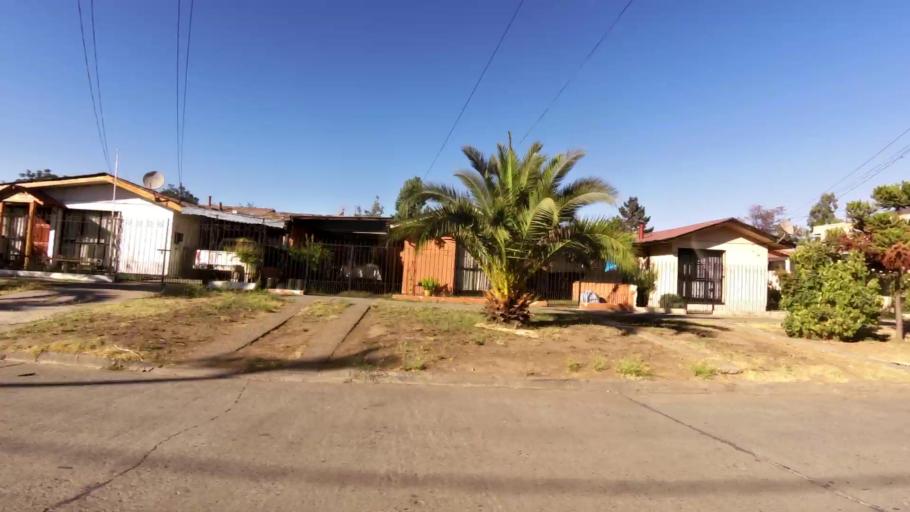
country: CL
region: O'Higgins
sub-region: Provincia de Cachapoal
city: Rancagua
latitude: -34.1758
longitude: -70.7219
